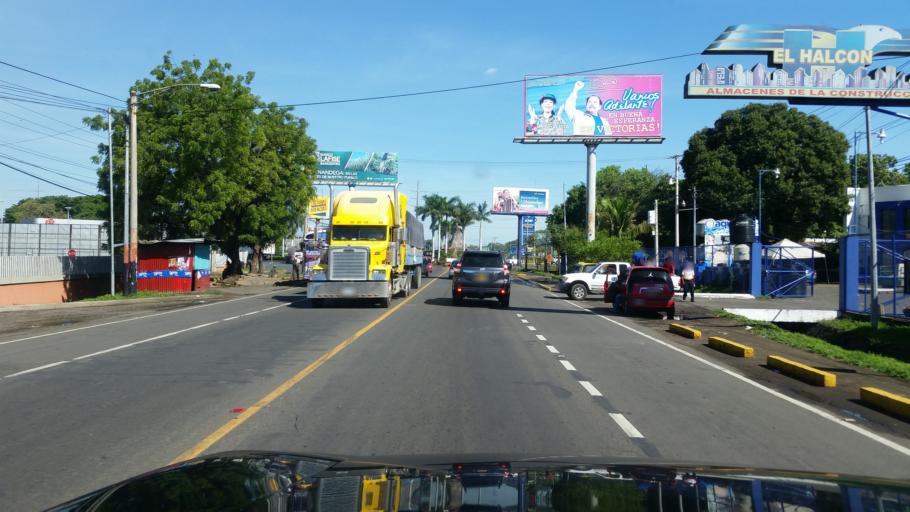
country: NI
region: Chinandega
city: Chinandega
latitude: 12.6225
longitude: -87.1188
